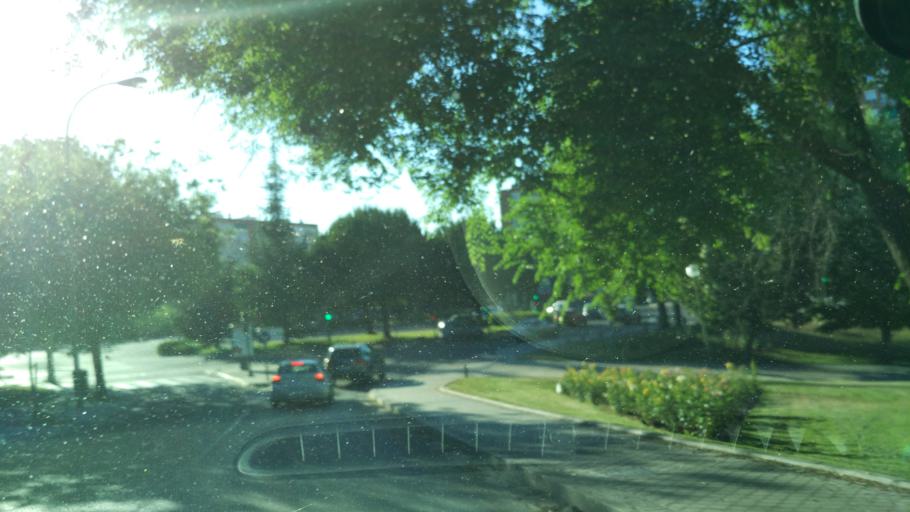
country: ES
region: Madrid
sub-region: Provincia de Madrid
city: Tetuan de las Victorias
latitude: 40.4703
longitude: -3.7111
